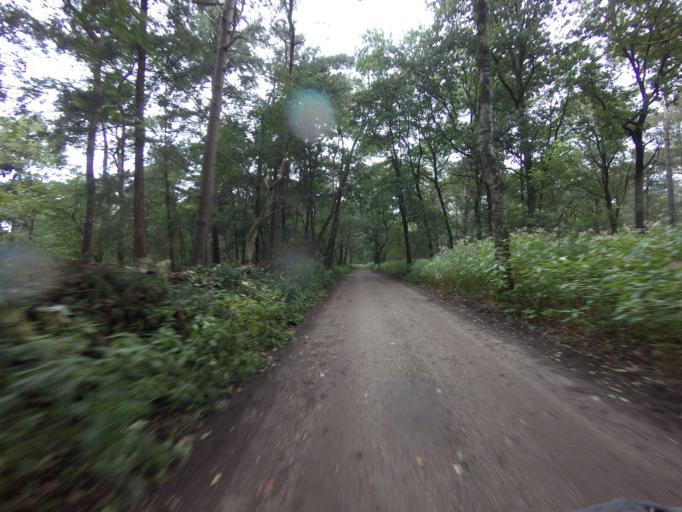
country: NL
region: Utrecht
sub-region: Gemeente Soest
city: Soest
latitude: 52.1516
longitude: 5.3330
